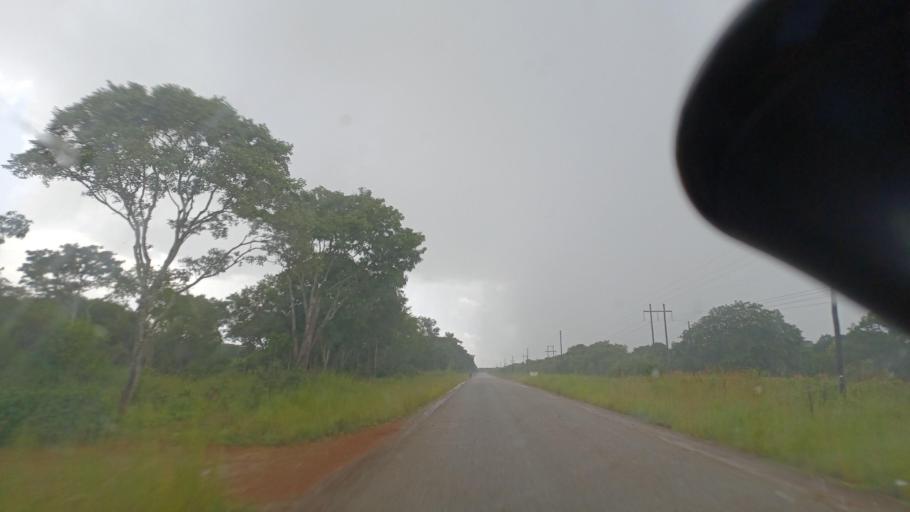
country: ZM
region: North-Western
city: Kasempa
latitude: -13.0912
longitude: 25.9373
